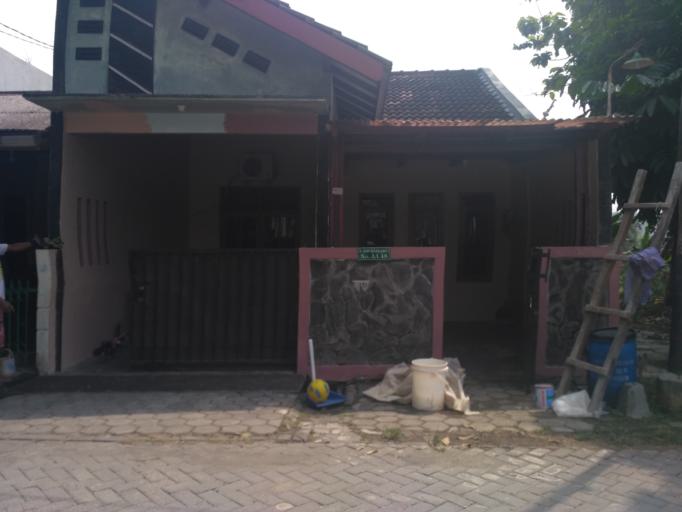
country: ID
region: Central Java
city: Mranggen
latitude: -7.0641
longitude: 110.4598
